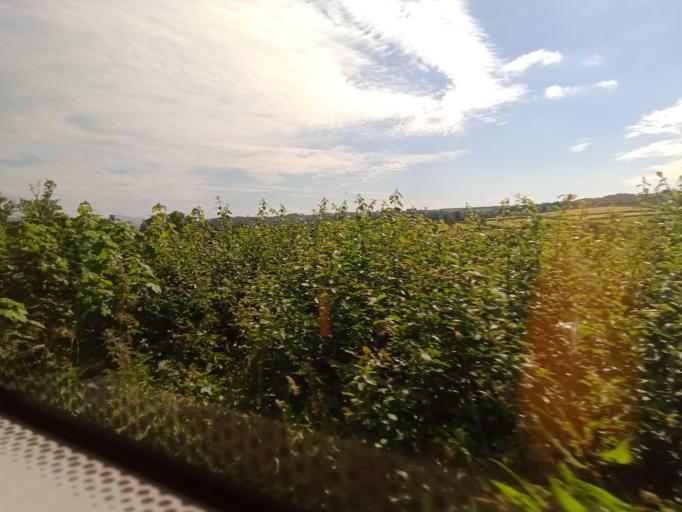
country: GB
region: Wales
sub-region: Anglesey
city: Llangoed
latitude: 53.3001
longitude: -4.0837
